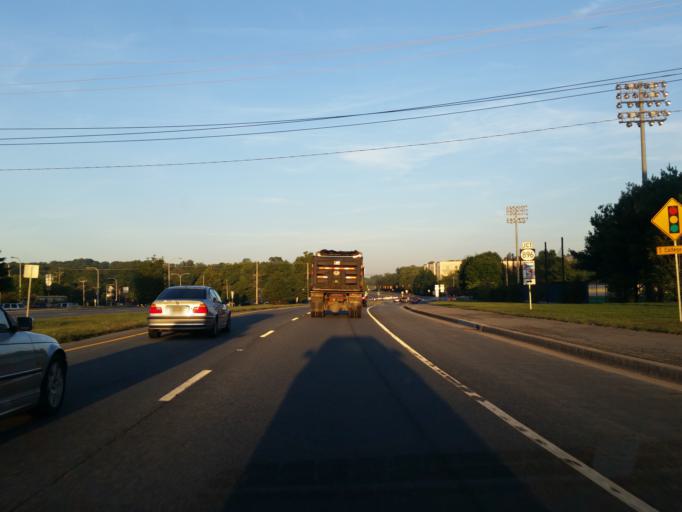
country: US
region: Delaware
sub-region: New Castle County
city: Brookside
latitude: 39.6584
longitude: -75.7483
